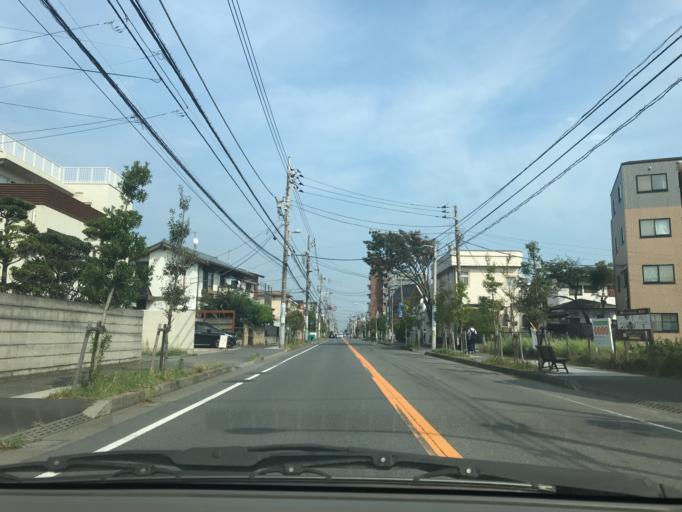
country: JP
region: Kanagawa
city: Chigasaki
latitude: 35.3249
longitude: 139.4118
